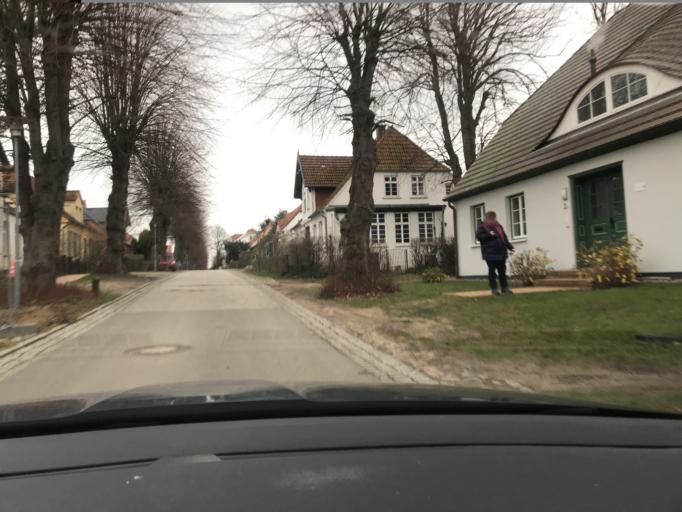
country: DE
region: Mecklenburg-Vorpommern
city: Ostseebad Dierhagen
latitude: 54.3459
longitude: 12.3929
